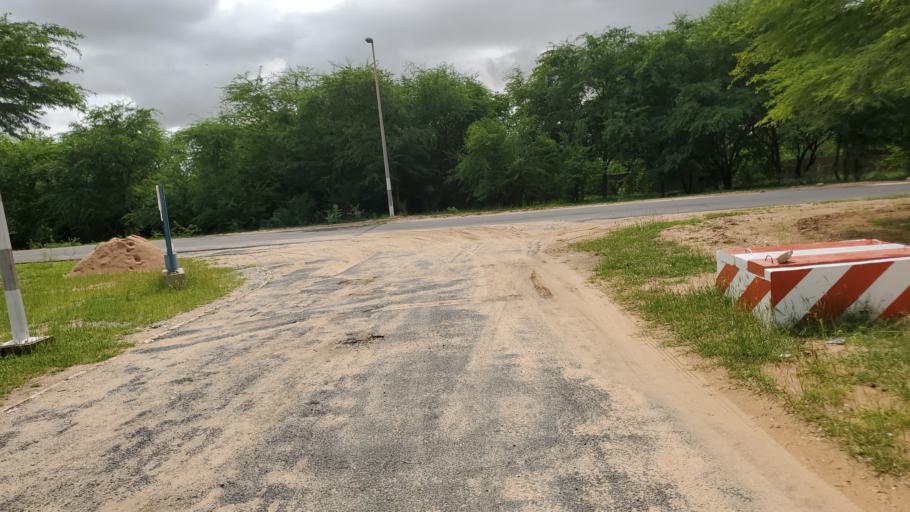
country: SN
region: Saint-Louis
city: Saint-Louis
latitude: 16.0615
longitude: -16.4282
